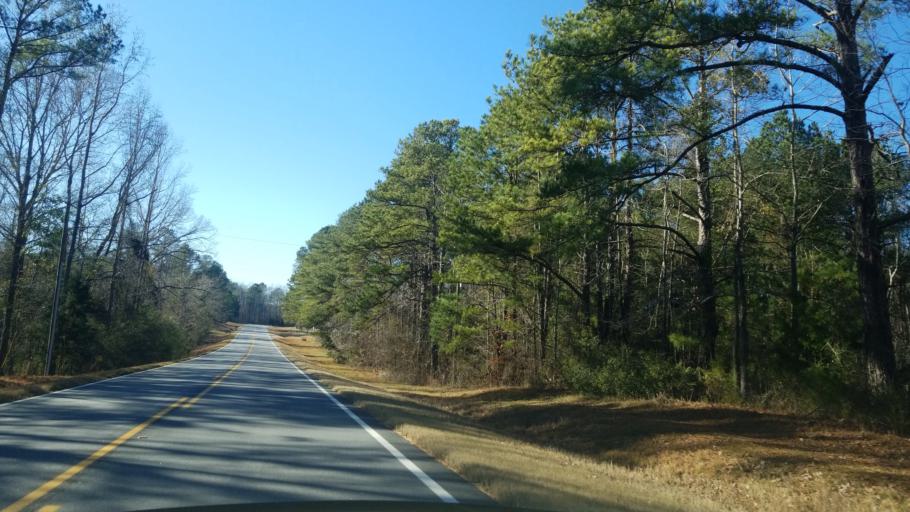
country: US
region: Georgia
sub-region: Harris County
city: Hamilton
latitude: 32.6675
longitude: -84.8864
